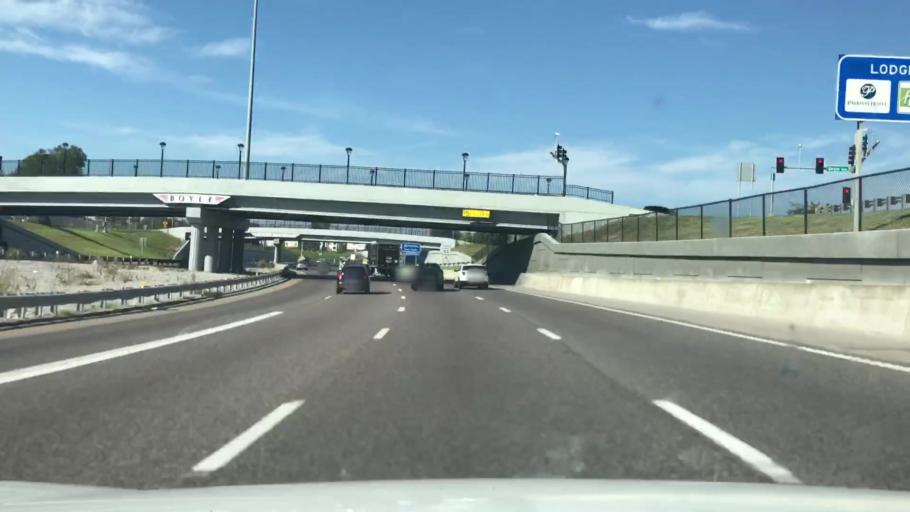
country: US
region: Missouri
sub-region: City of Saint Louis
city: St. Louis
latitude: 38.6314
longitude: -90.2525
